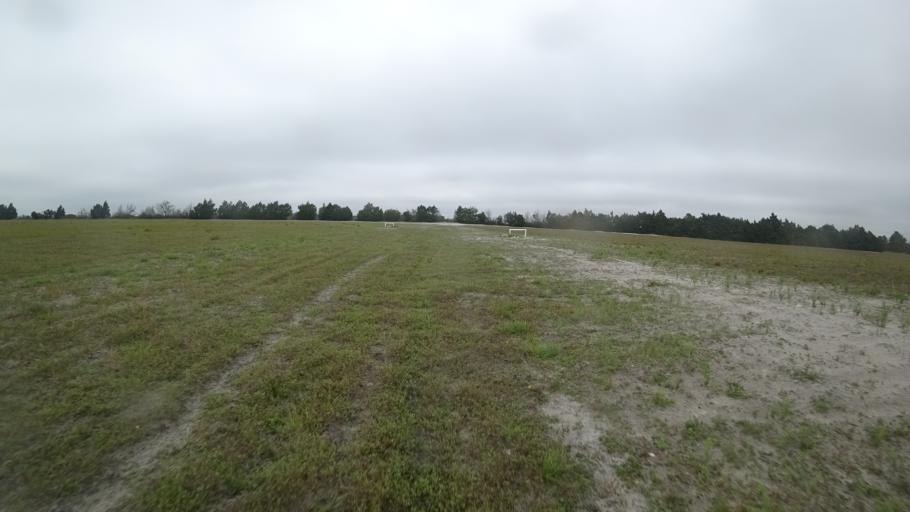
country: US
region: Florida
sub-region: Sarasota County
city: Warm Mineral Springs
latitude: 27.3077
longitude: -82.1532
